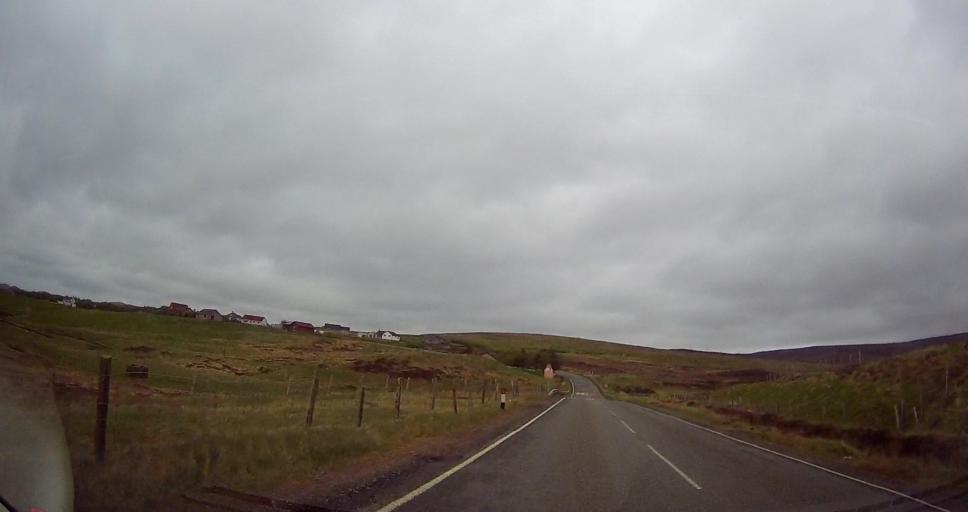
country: GB
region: Scotland
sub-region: Shetland Islands
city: Lerwick
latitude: 60.3827
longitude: -1.3426
